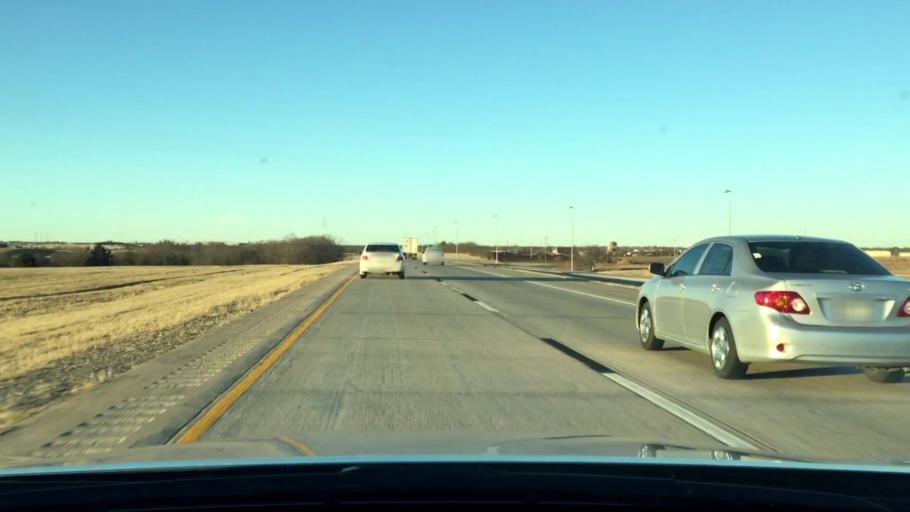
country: US
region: Oklahoma
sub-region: Love County
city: Marietta
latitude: 33.9076
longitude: -97.1340
